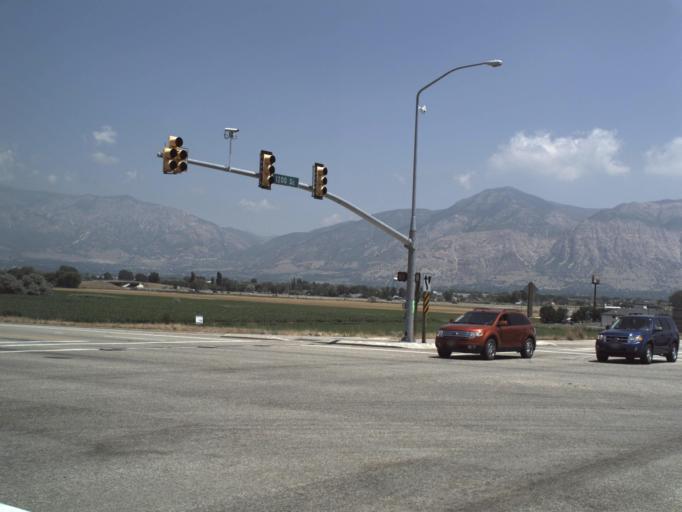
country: US
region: Utah
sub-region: Weber County
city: Marriott-Slaterville
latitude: 41.2450
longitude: -112.0286
